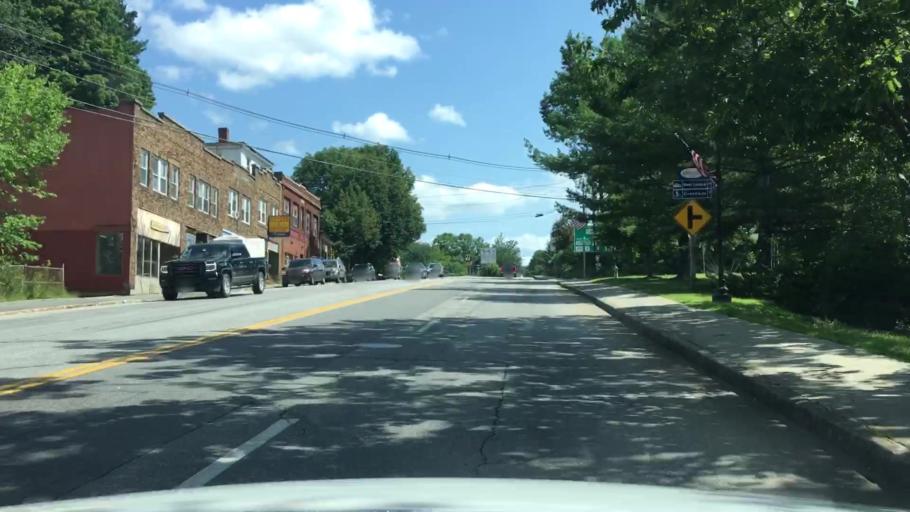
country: US
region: Maine
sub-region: Kennebec County
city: Augusta
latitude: 44.3165
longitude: -69.7702
